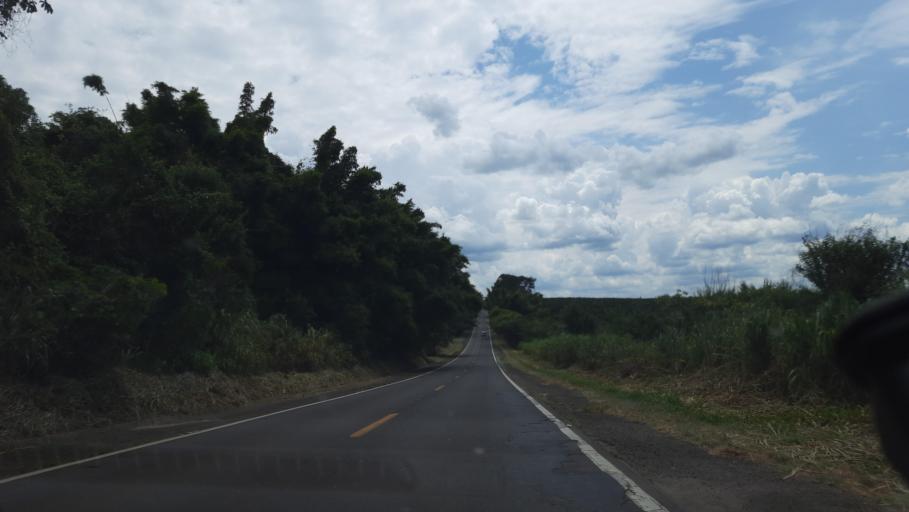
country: BR
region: Sao Paulo
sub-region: Mococa
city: Mococa
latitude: -21.5013
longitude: -47.0589
